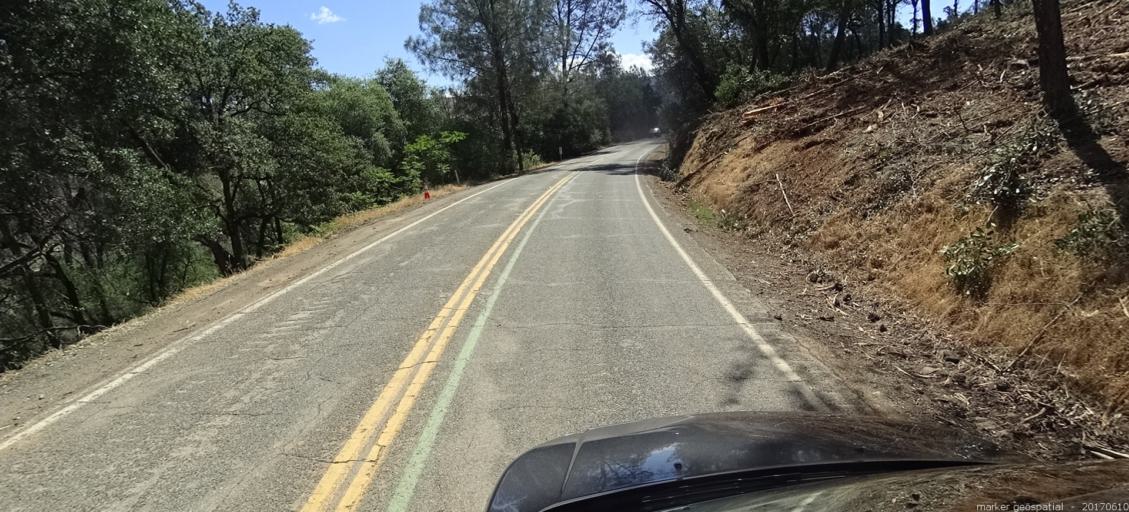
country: US
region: California
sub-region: Butte County
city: Oroville East
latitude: 39.5346
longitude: -121.5064
